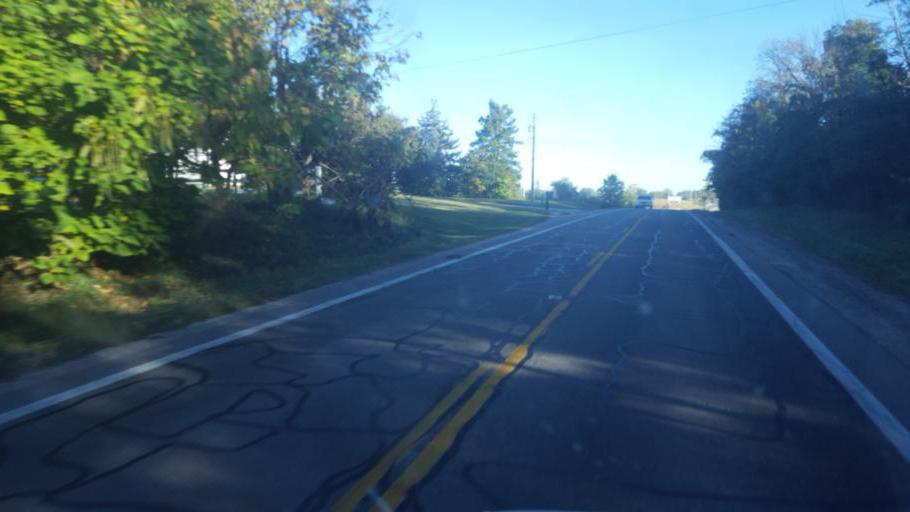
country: US
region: Ohio
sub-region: Morrow County
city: Mount Gilead
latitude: 40.6373
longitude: -82.8225
